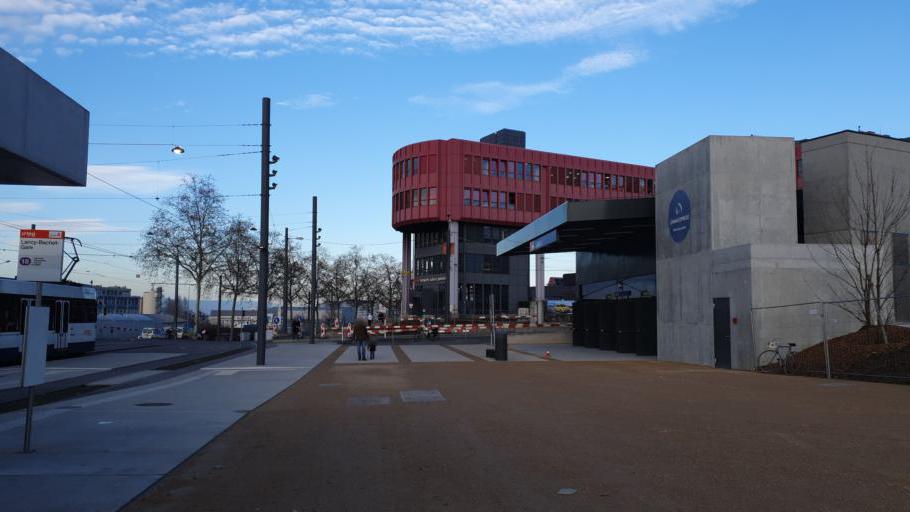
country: CH
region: Geneva
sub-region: Geneva
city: Carouge
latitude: 46.1738
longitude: 6.1300
